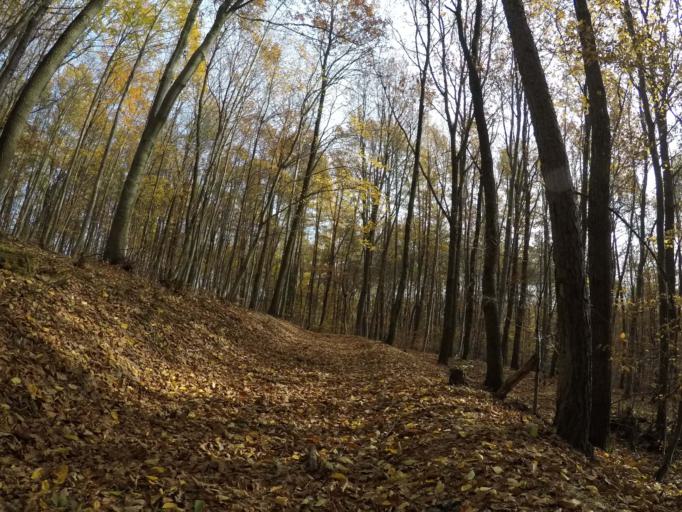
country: SK
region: Presovsky
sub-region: Okres Presov
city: Presov
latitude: 48.9203
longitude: 21.2256
